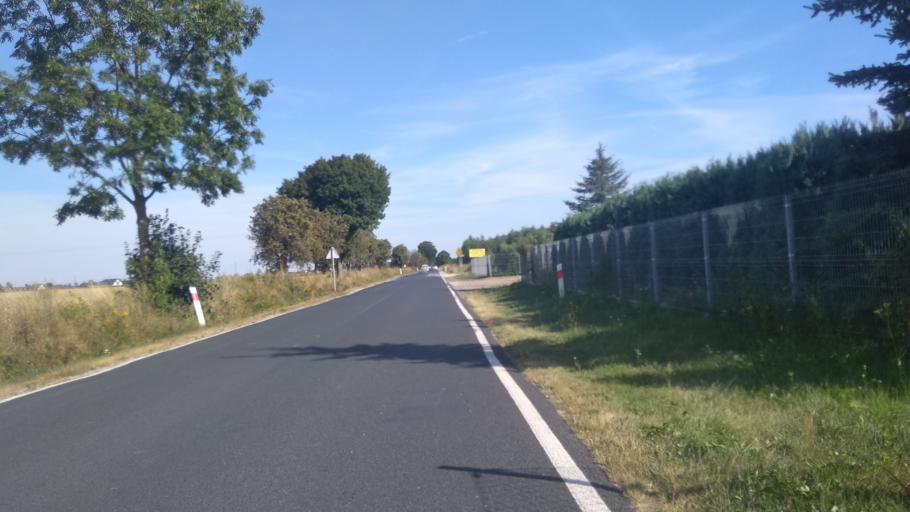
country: PL
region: Kujawsko-Pomorskie
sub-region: Powiat bydgoski
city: Osielsko
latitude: 53.2183
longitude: 18.1370
